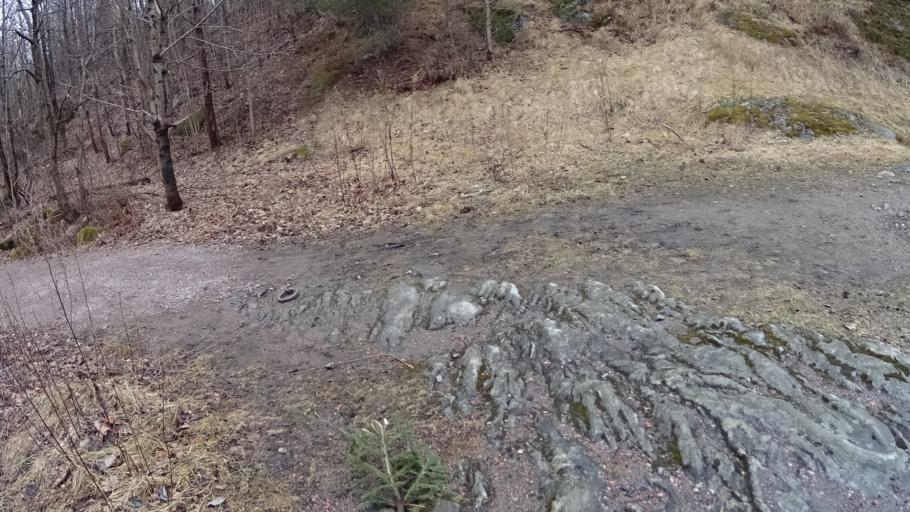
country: FI
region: Uusimaa
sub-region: Helsinki
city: Teekkarikylae
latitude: 60.2949
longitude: 24.8660
